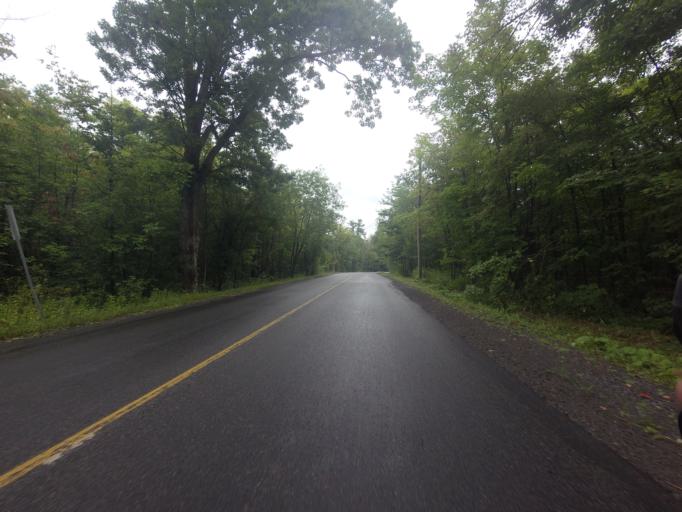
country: CA
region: Ontario
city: Bells Corners
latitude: 45.3467
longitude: -75.9602
